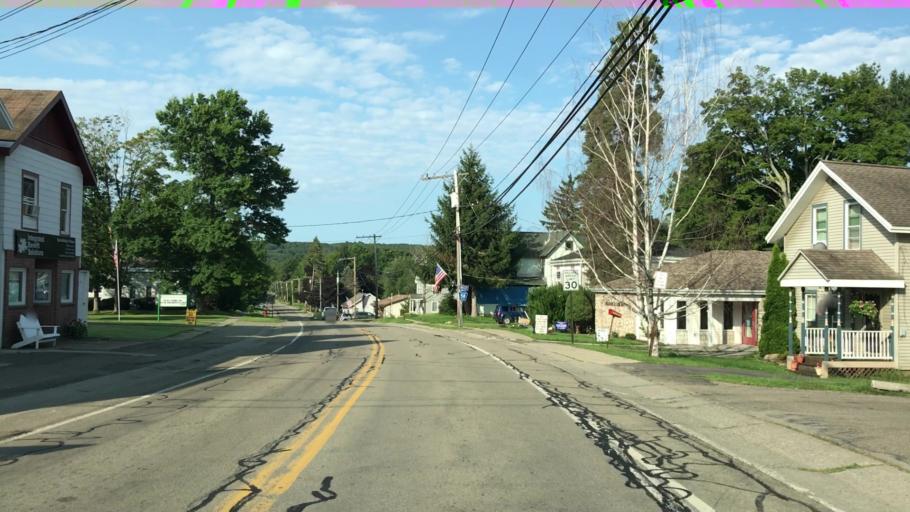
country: US
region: New York
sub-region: Chautauqua County
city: Fredonia
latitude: 42.3443
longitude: -79.3101
